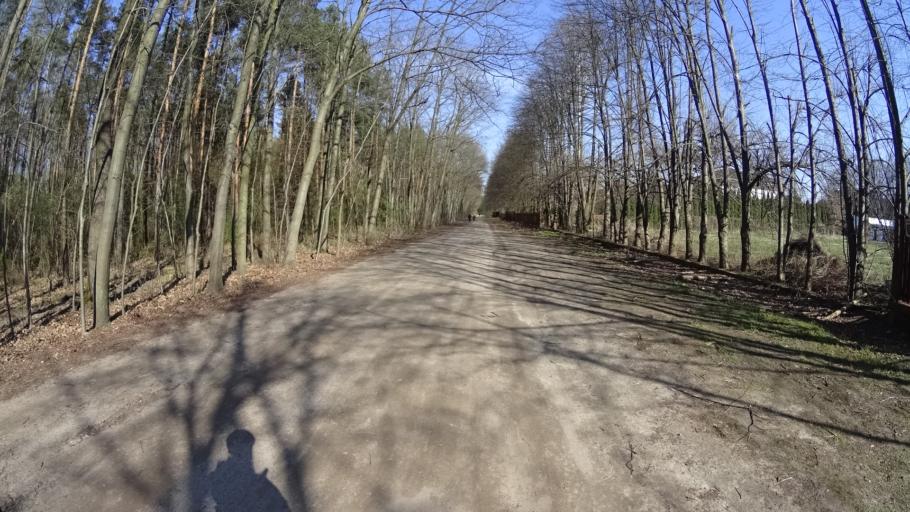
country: PL
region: Masovian Voivodeship
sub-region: Powiat warszawski zachodni
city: Babice
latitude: 52.2549
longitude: 20.8587
